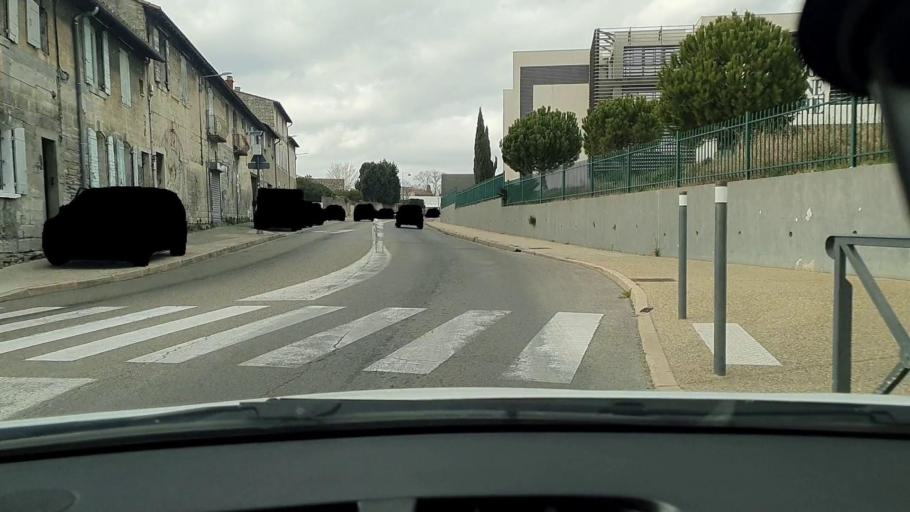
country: FR
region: Languedoc-Roussillon
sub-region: Departement du Gard
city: Beaucaire
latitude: 43.8097
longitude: 4.6385
